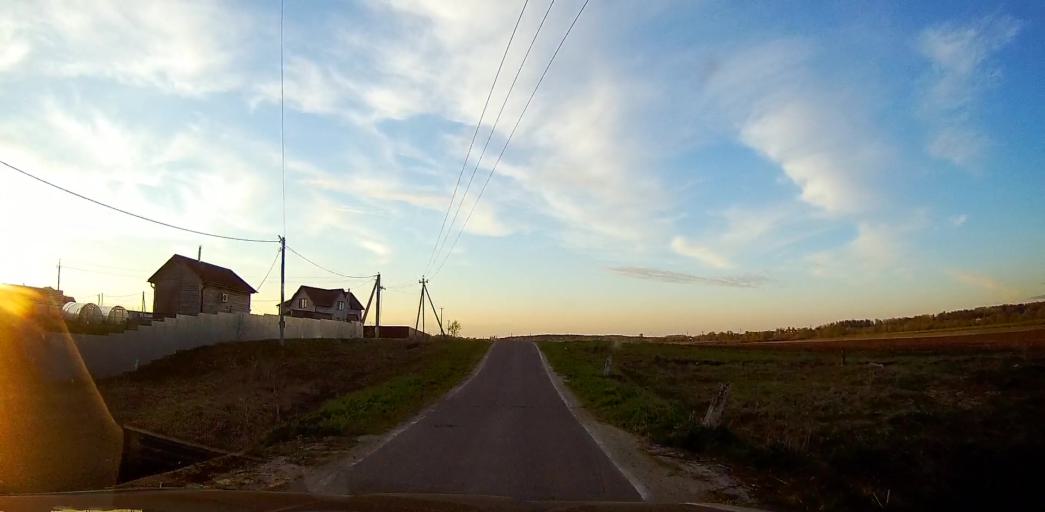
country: RU
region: Moskovskaya
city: Peski
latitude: 55.2137
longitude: 38.7390
